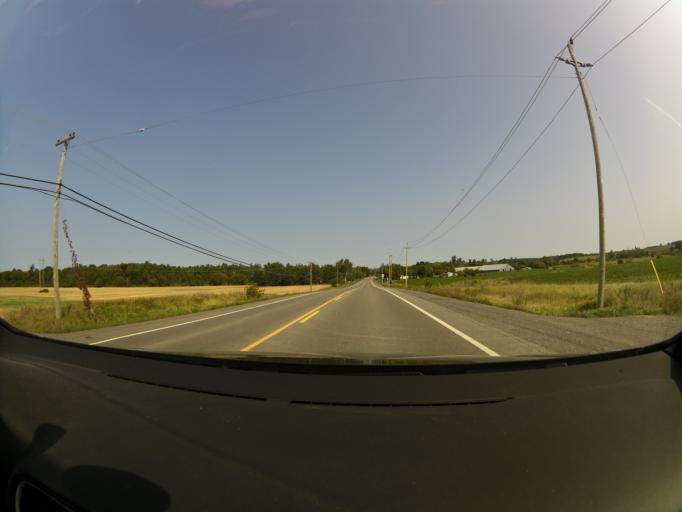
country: CA
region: Ontario
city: Arnprior
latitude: 45.4205
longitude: -76.2620
